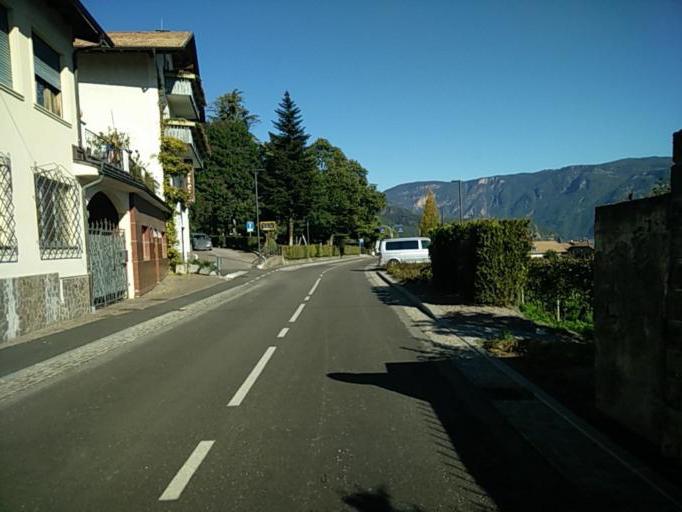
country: IT
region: Trentino-Alto Adige
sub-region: Bolzano
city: Termeno
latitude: 46.3433
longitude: 11.2473
